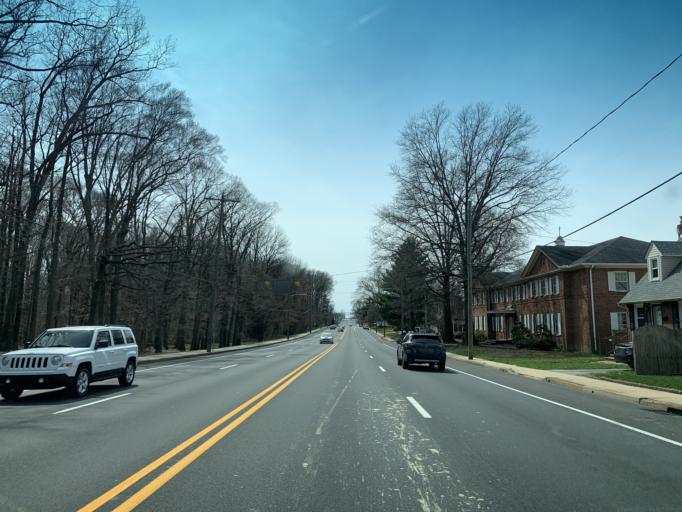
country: US
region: Delaware
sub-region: New Castle County
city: Newport
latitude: 39.7210
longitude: -75.5968
